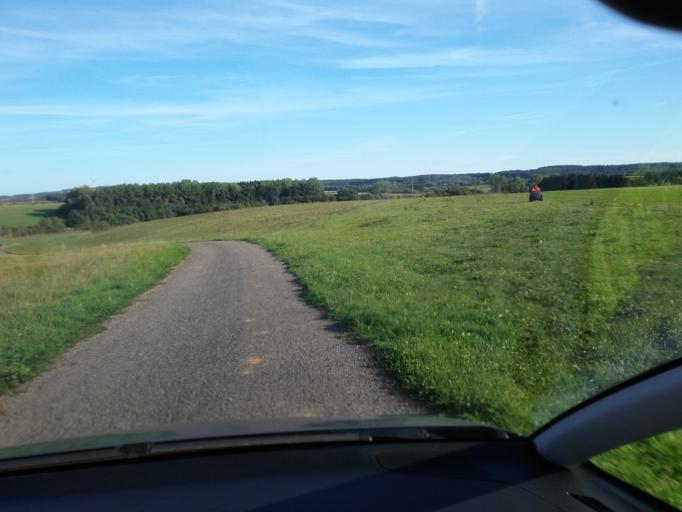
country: BE
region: Wallonia
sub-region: Province du Luxembourg
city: Habay-la-Vieille
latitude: 49.7084
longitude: 5.7011
